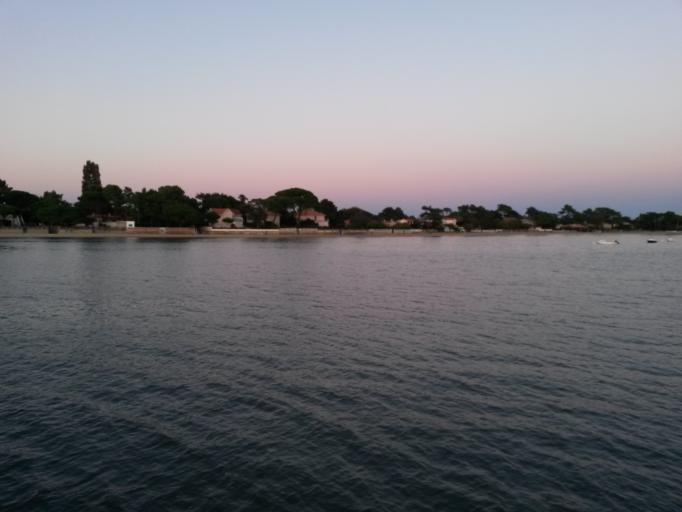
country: FR
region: Aquitaine
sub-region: Departement de la Gironde
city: Andernos-les-Bains
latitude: 44.7378
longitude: -1.1020
